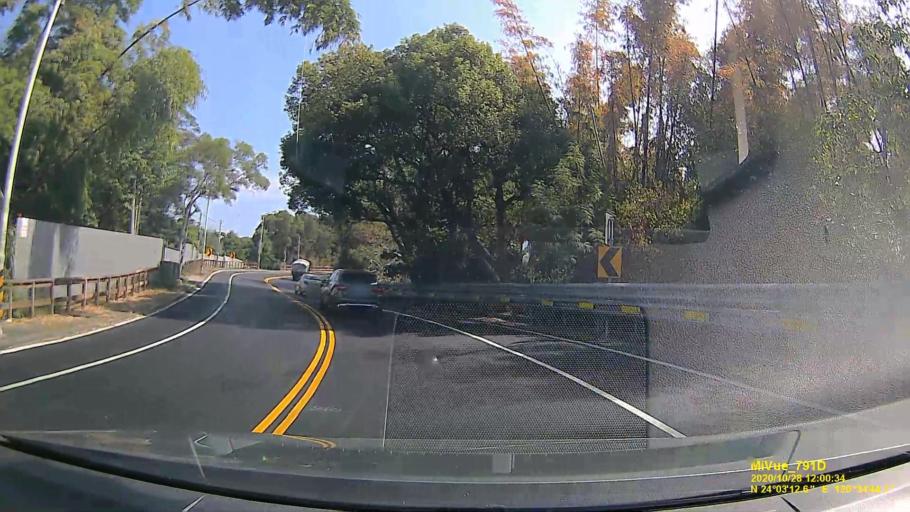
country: TW
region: Taiwan
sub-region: Changhua
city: Chang-hua
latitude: 24.0535
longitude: 120.5791
